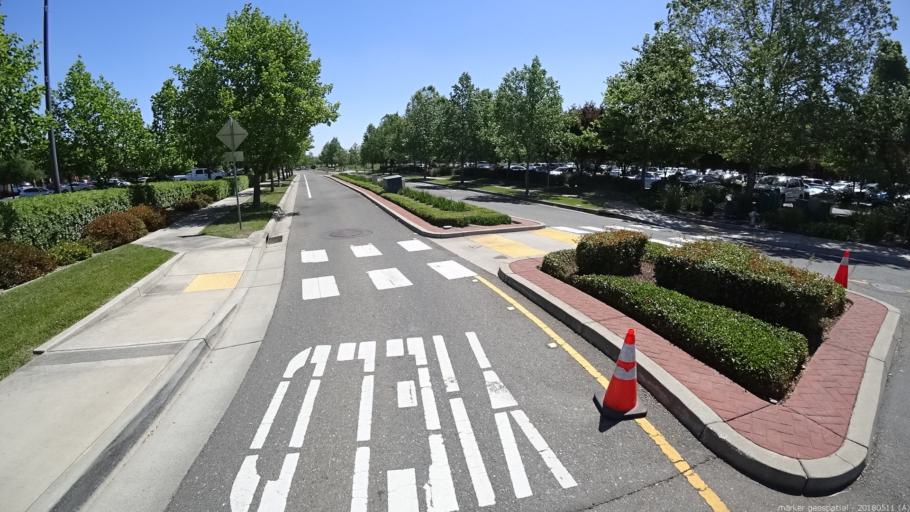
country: US
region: California
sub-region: Sacramento County
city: Sacramento
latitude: 38.6374
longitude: -121.4993
